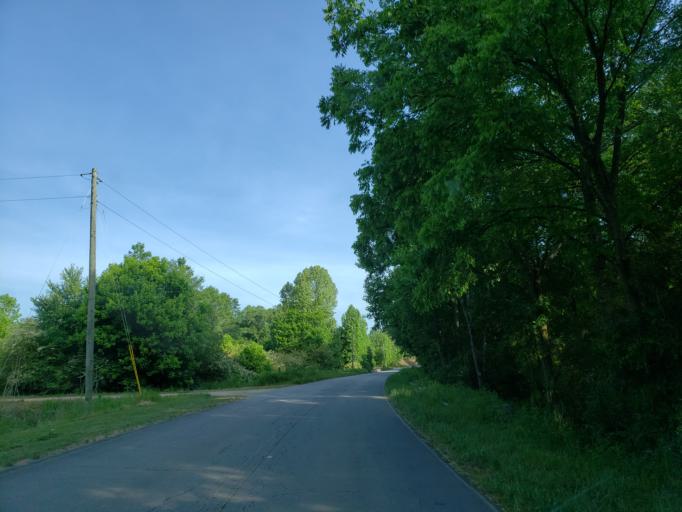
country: US
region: Georgia
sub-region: Carroll County
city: Bowdon
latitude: 33.4852
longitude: -85.3024
